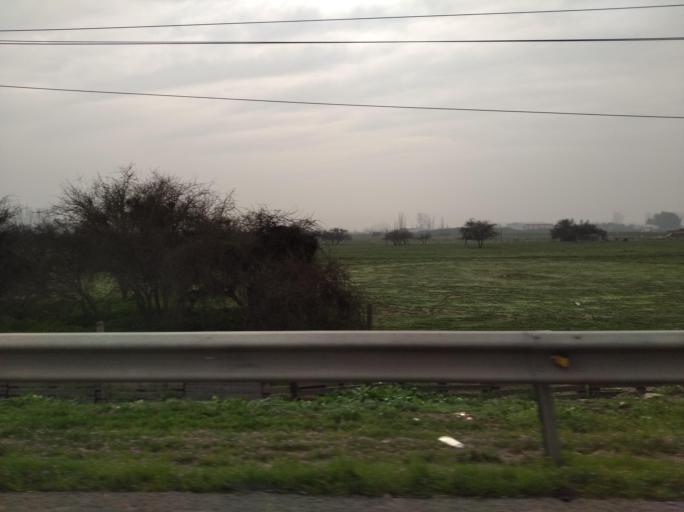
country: CL
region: Santiago Metropolitan
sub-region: Provincia de Chacabuco
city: Lampa
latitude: -33.3322
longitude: -70.8207
